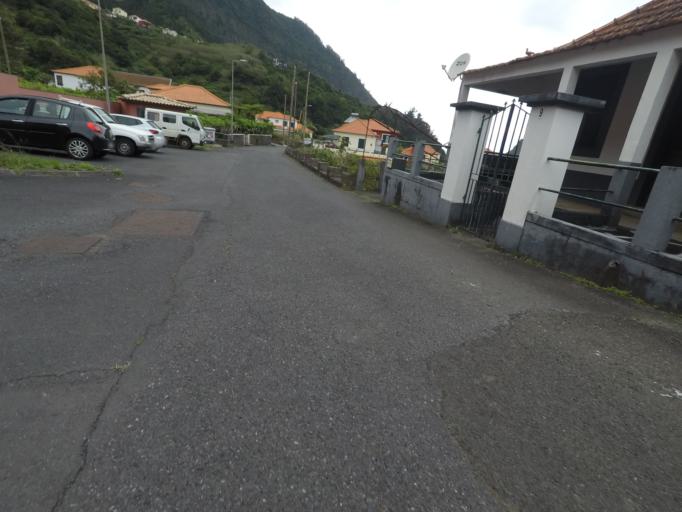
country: PT
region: Madeira
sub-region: Sao Vicente
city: Sao Vicente
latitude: 32.7938
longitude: -17.0416
